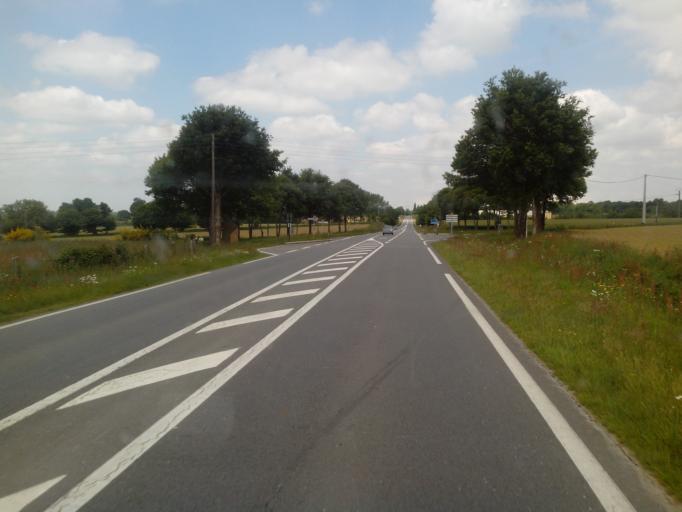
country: FR
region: Brittany
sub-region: Departement d'Ille-et-Vilaine
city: Saint-Germain-en-Cogles
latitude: 48.3853
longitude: -1.2728
